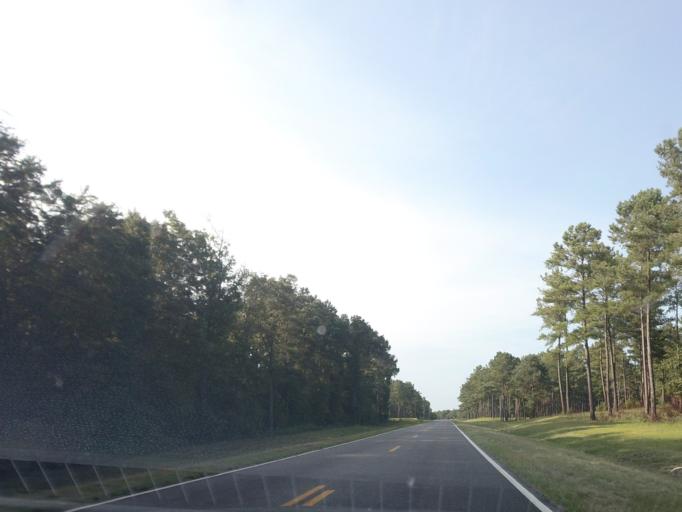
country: US
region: Georgia
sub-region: Bleckley County
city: Cochran
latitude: 32.4620
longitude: -83.2986
